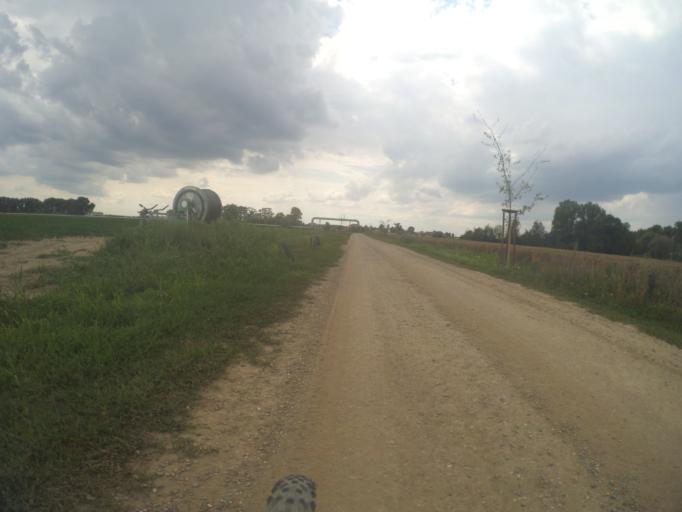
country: CZ
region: Central Bohemia
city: Luzec nad Vltavou
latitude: 50.3104
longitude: 14.4463
